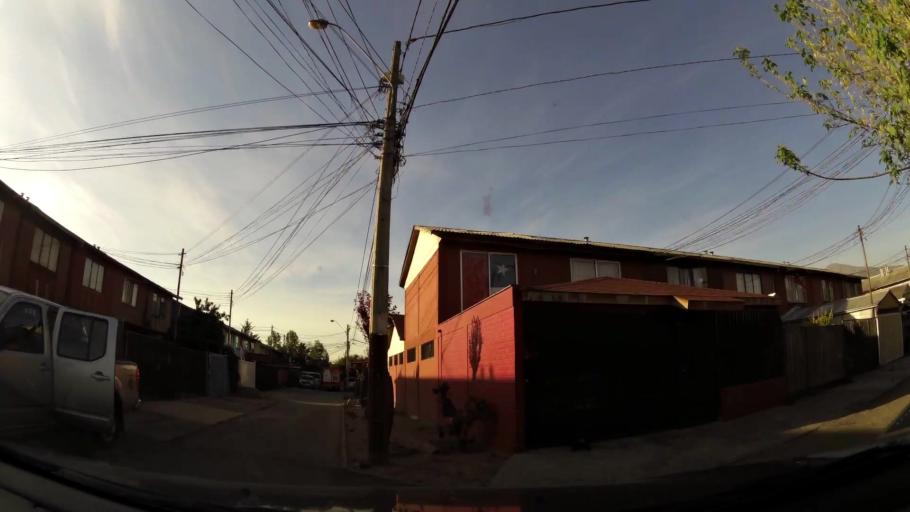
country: CL
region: Santiago Metropolitan
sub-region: Provincia de Cordillera
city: Puente Alto
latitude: -33.5981
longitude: -70.5611
